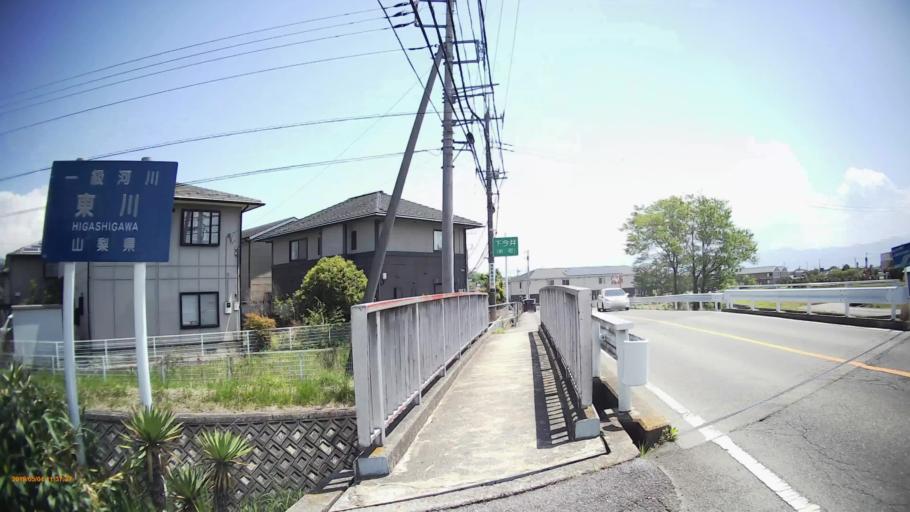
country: JP
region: Yamanashi
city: Nirasaki
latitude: 35.6882
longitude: 138.4843
